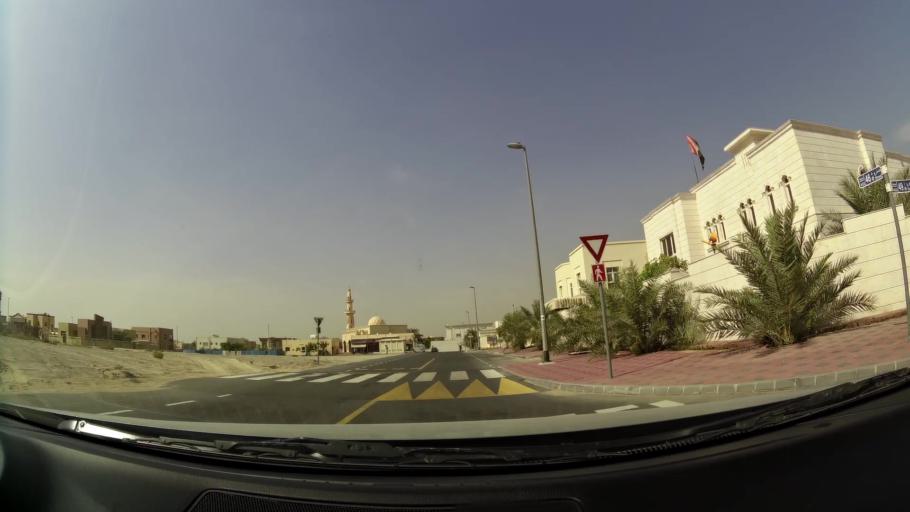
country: AE
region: Ash Shariqah
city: Sharjah
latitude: 25.2067
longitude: 55.4166
